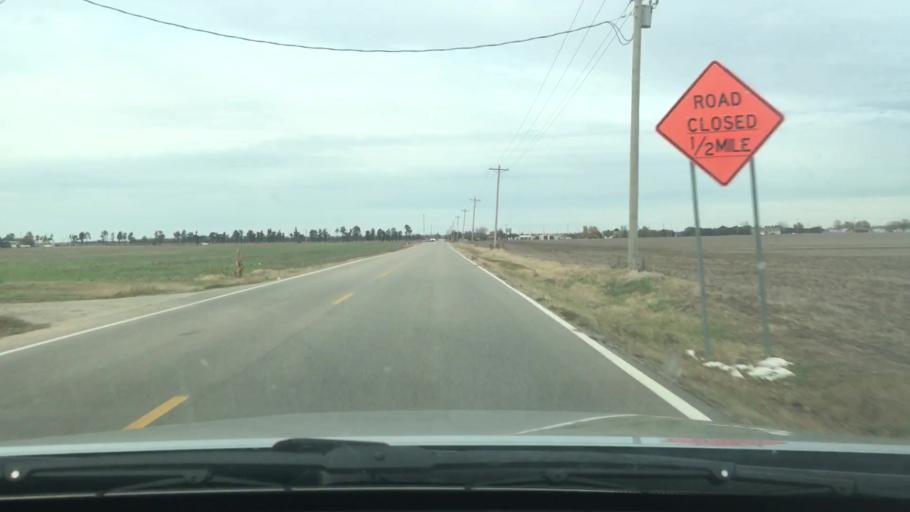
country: US
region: Kansas
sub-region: Sedgwick County
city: Maize
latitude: 37.7731
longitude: -97.4994
